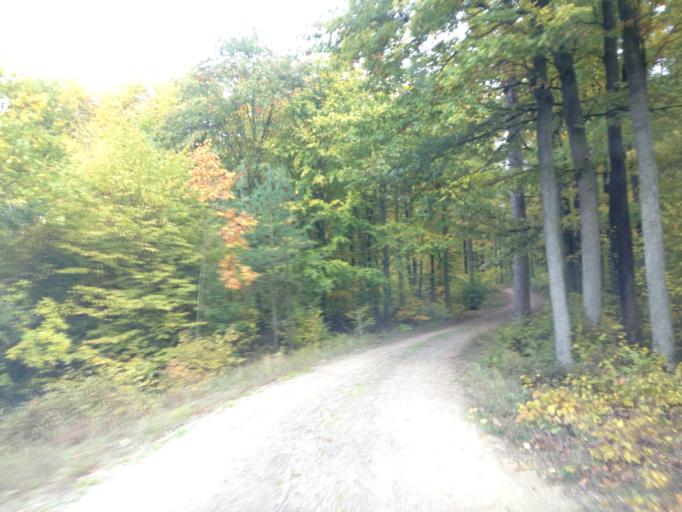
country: PL
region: Kujawsko-Pomorskie
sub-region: Powiat brodnicki
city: Gorzno
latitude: 53.2671
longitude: 19.7103
